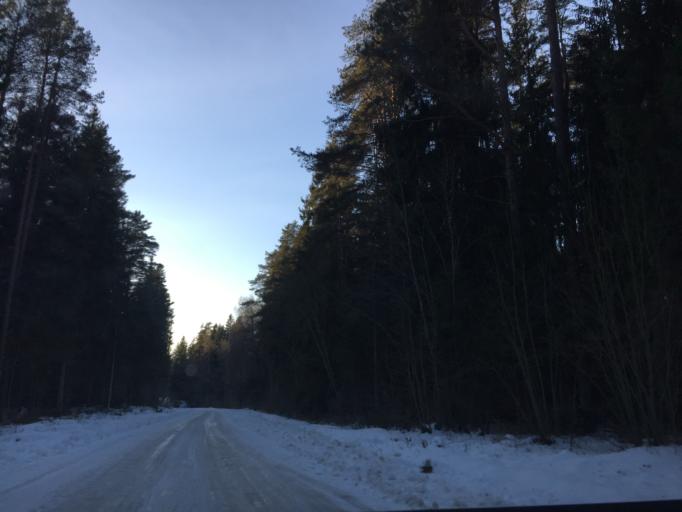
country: LV
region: Ogre
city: Jumprava
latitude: 56.6316
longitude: 24.9082
